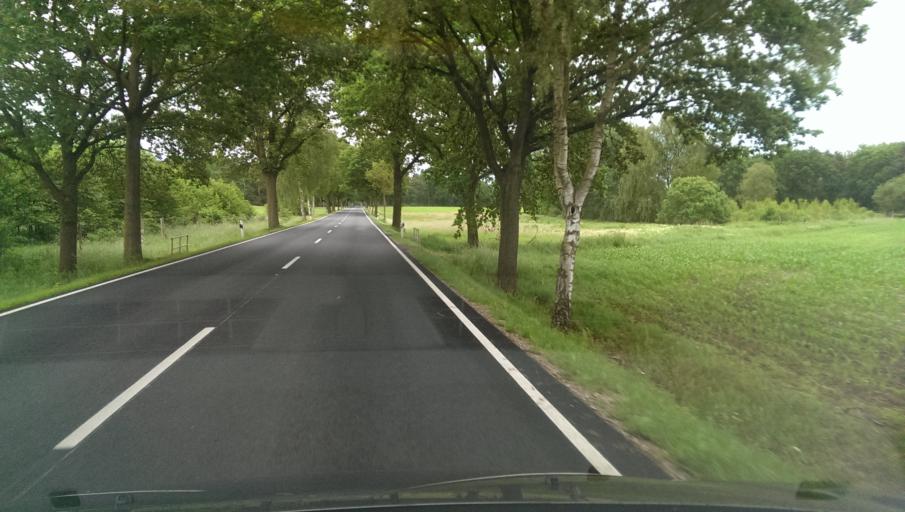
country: DE
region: Lower Saxony
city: Tulau
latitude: 52.6255
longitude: 10.8892
